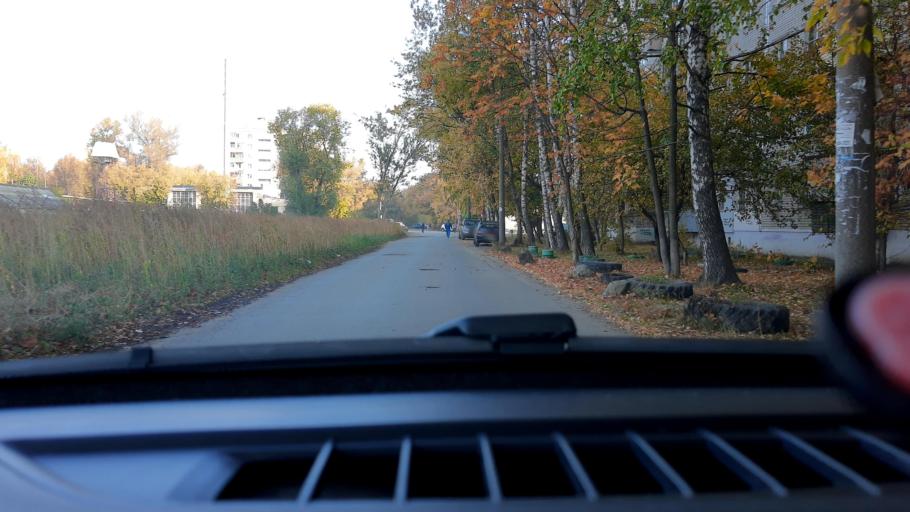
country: RU
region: Nizjnij Novgorod
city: Nizhniy Novgorod
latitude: 56.3100
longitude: 43.8862
